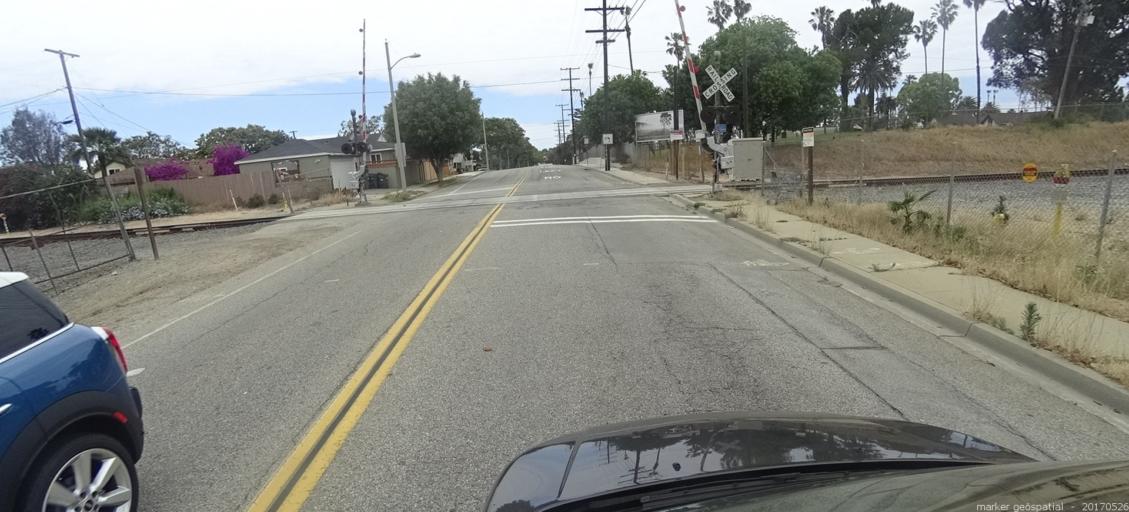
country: US
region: California
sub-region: Los Angeles County
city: Lawndale
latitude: 33.8656
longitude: -118.3585
